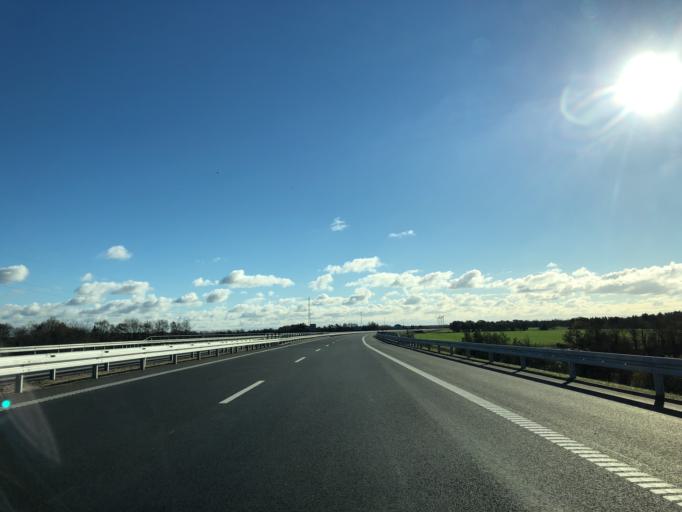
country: DK
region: Central Jutland
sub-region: Holstebro Kommune
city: Holstebro
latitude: 56.3647
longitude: 8.7257
